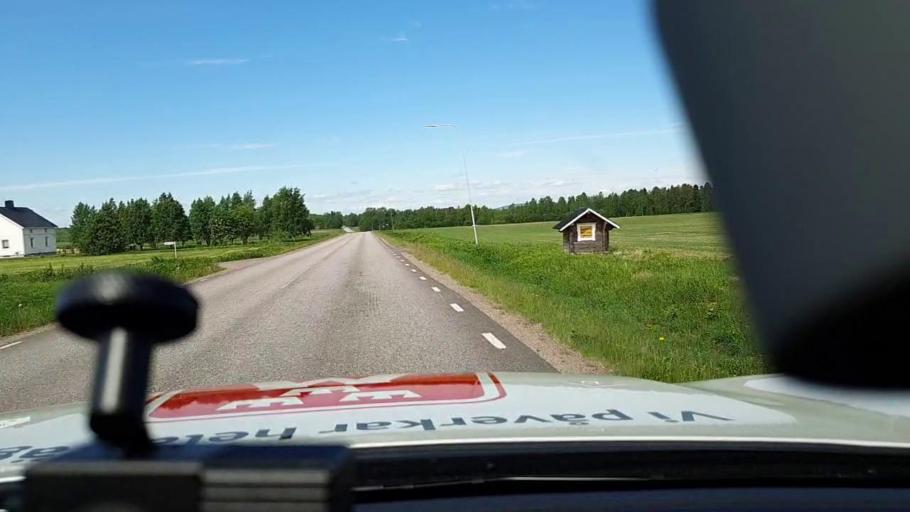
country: SE
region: Norrbotten
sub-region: Lulea Kommun
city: Sodra Sunderbyn
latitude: 65.6506
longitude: 21.8699
